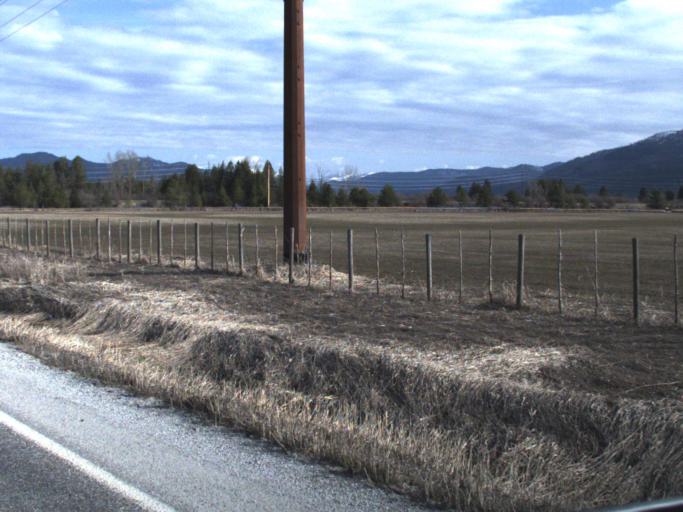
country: US
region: Washington
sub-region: Pend Oreille County
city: Newport
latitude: 48.3835
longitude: -117.3098
